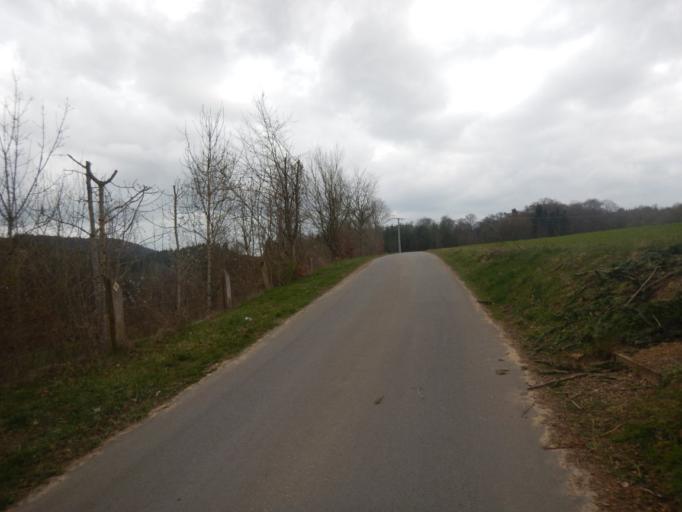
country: LU
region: Luxembourg
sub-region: Canton de Mersch
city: Lorentzweiler
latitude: 49.7065
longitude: 6.1466
